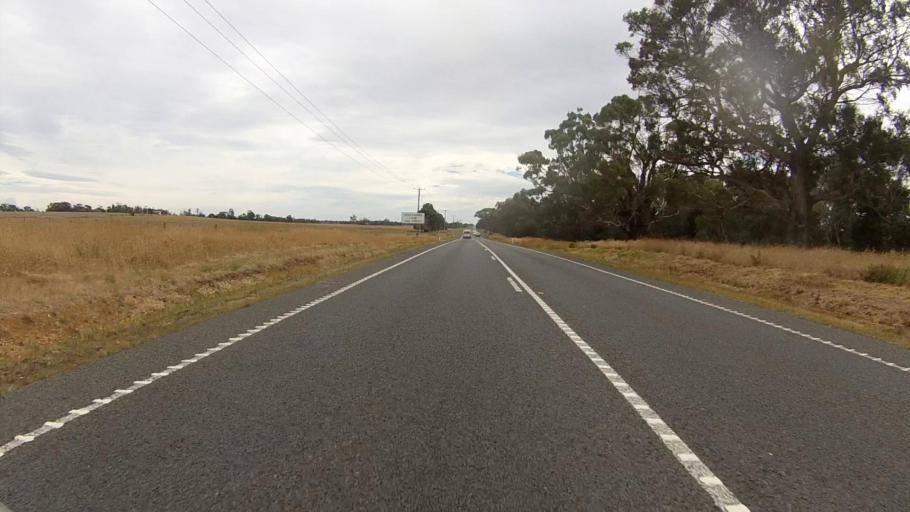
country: AU
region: Tasmania
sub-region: Northern Midlands
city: Evandale
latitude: -41.6981
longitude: 147.2894
